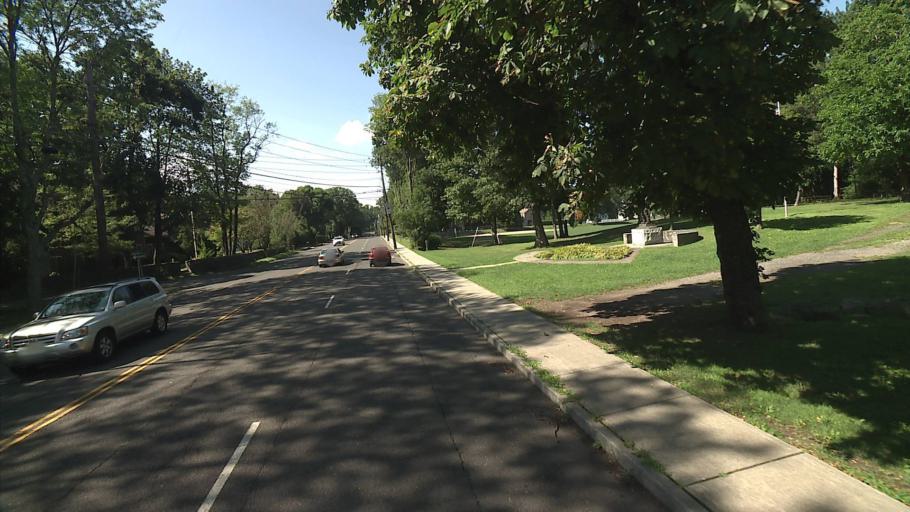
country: US
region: Connecticut
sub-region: Fairfield County
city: Darien
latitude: 41.0661
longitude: -73.4799
